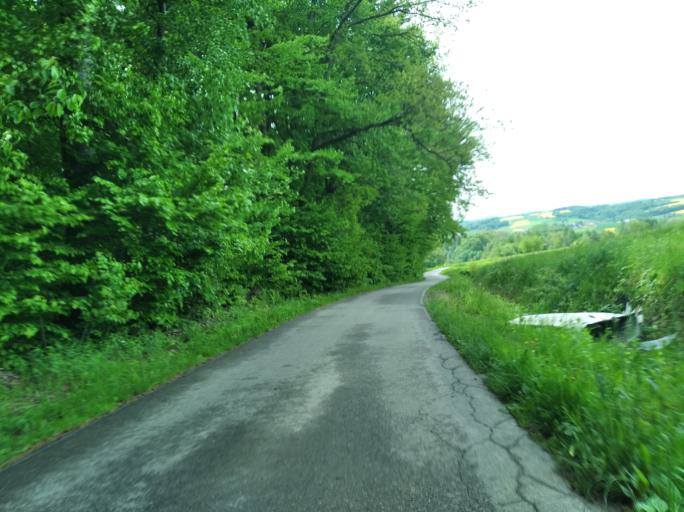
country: PL
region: Subcarpathian Voivodeship
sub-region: Powiat strzyzowski
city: Wisniowa
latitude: 49.9305
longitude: 21.7159
